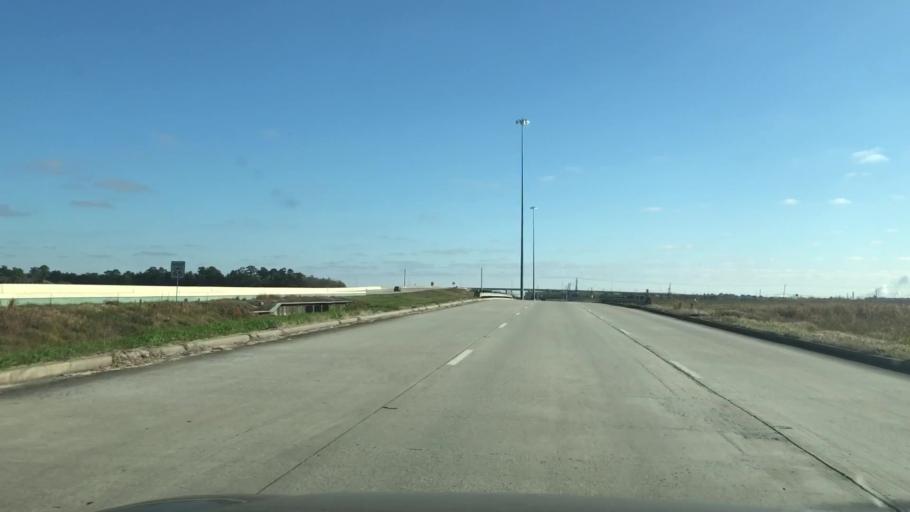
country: US
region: Texas
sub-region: Harris County
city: Cloverleaf
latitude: 29.8268
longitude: -95.1876
